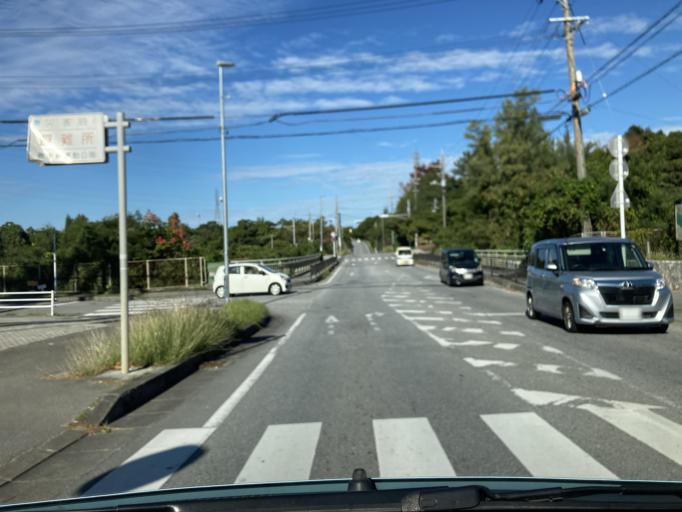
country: JP
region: Okinawa
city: Okinawa
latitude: 26.3701
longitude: 127.7705
